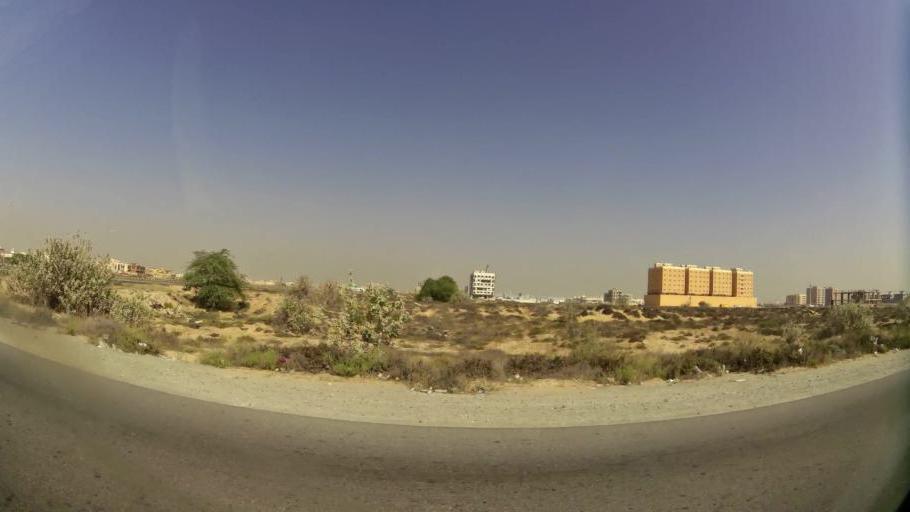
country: AE
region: Ajman
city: Ajman
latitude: 25.4208
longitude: 55.5386
